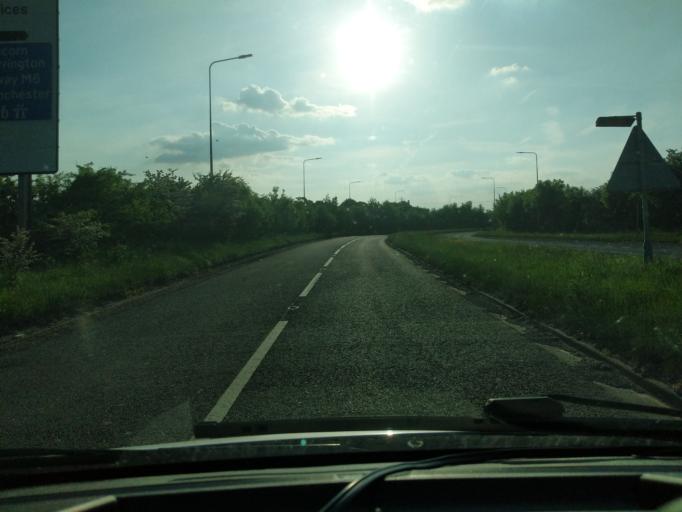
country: GB
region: England
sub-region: Cheshire West and Chester
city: Elton
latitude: 53.2648
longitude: -2.8003
